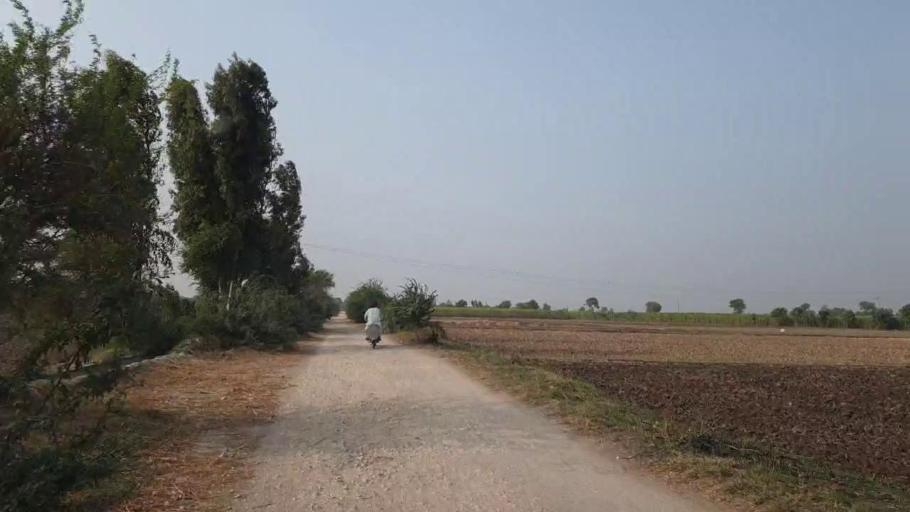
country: PK
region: Sindh
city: Tando Muhammad Khan
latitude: 25.0824
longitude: 68.5868
